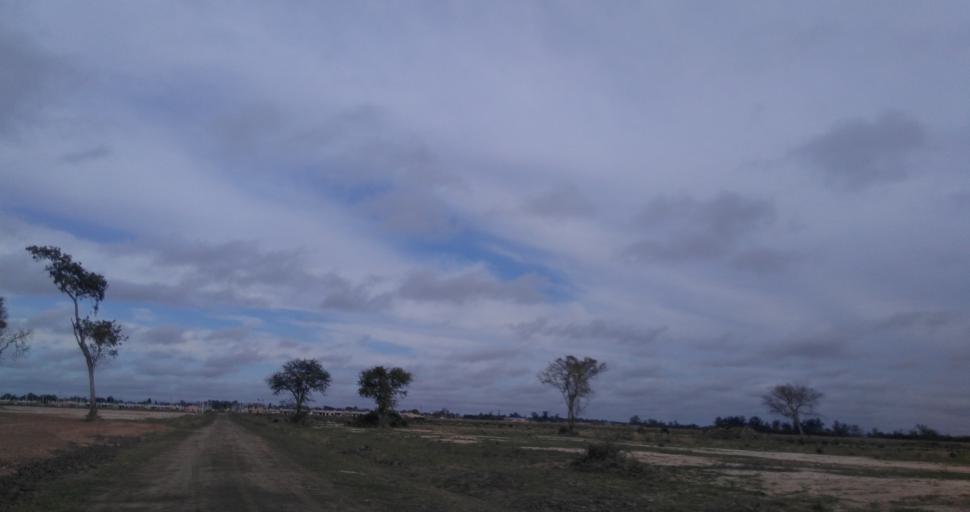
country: AR
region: Chaco
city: Fontana
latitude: -27.3910
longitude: -58.9838
